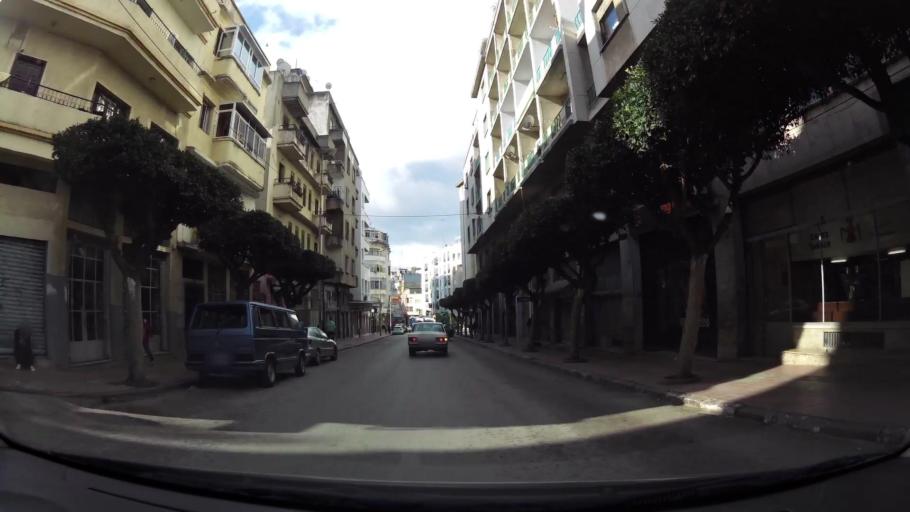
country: MA
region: Tanger-Tetouan
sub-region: Tanger-Assilah
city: Tangier
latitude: 35.7781
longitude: -5.8136
